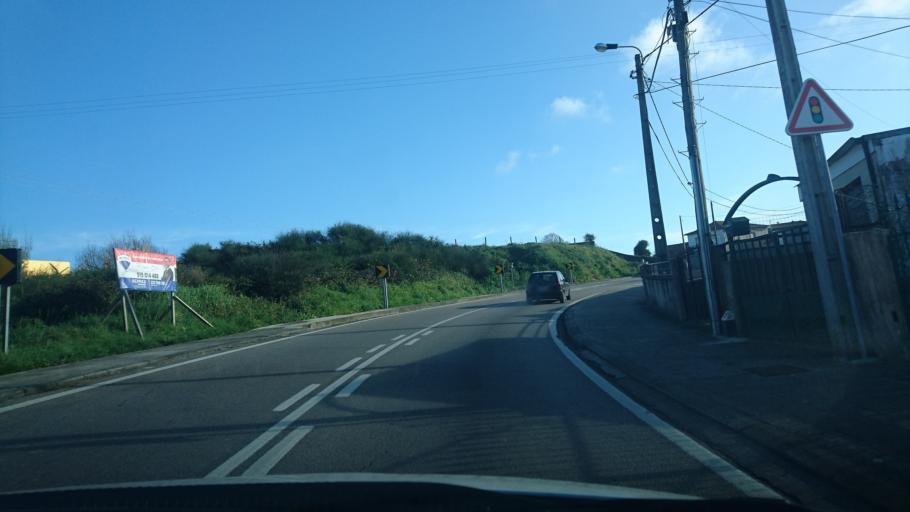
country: PT
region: Aveiro
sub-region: Espinho
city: Souto
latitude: 40.9764
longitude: -8.6301
